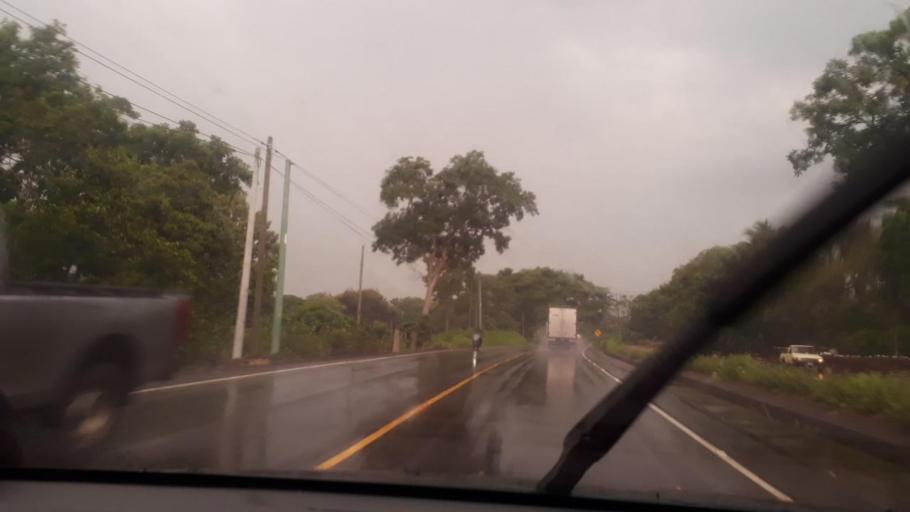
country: GT
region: Santa Rosa
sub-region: Municipio de Taxisco
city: Taxisco
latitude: 14.0900
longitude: -90.5085
